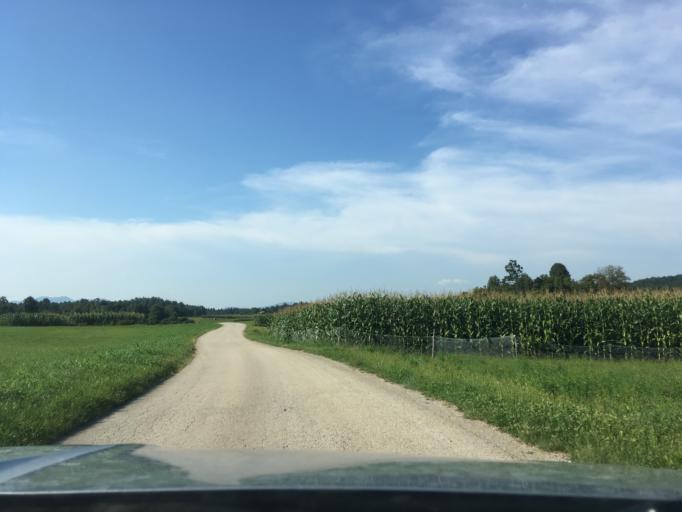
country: SI
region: Crnomelj
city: Crnomelj
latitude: 45.4709
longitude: 15.2092
